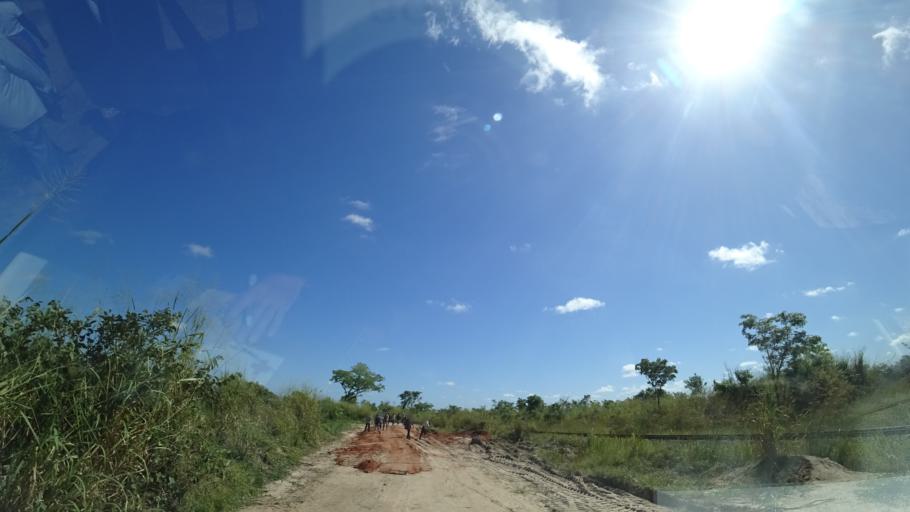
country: MZ
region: Sofala
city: Dondo
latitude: -19.2792
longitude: 34.6831
